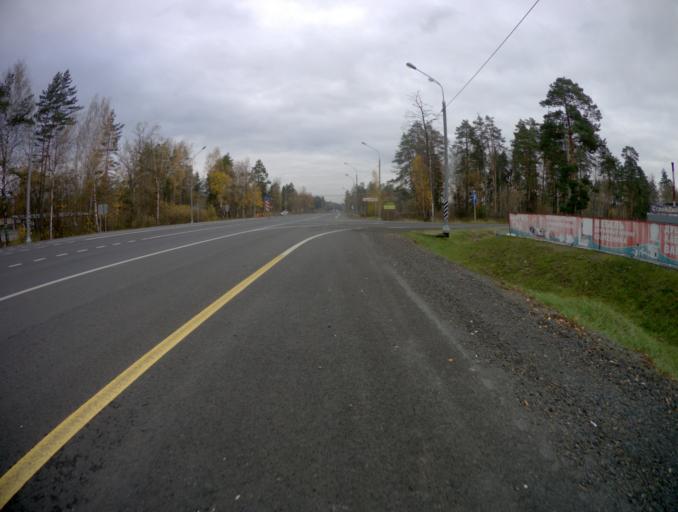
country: RU
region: Moskovskaya
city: Malaya Dubna
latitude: 55.8494
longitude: 38.9642
